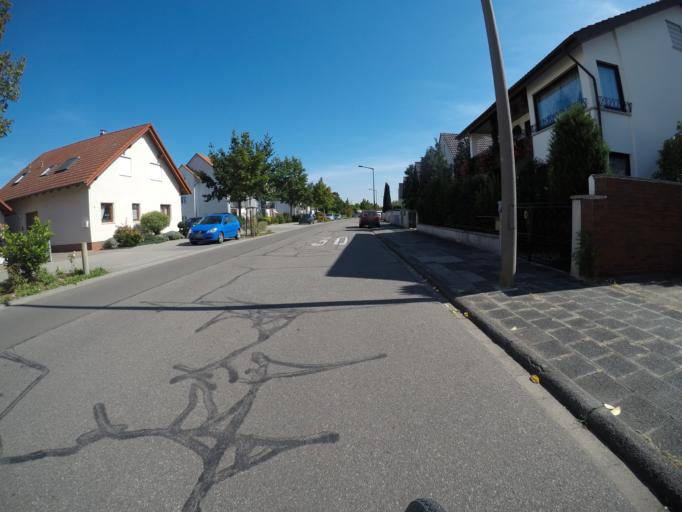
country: DE
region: Hesse
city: Lampertheim
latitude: 49.6047
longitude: 8.4727
